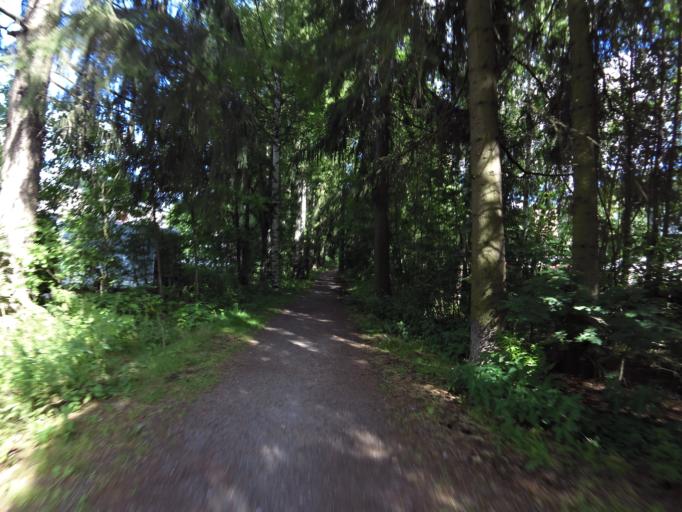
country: FI
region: Pirkanmaa
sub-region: Tampere
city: Yloejaervi
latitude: 61.5104
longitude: 23.6089
